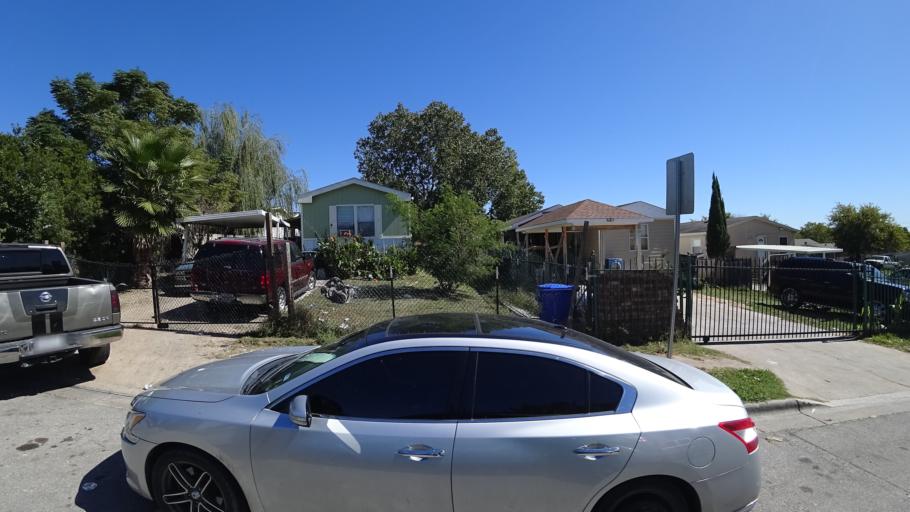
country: US
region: Texas
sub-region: Travis County
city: Hornsby Bend
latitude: 30.3081
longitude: -97.6392
